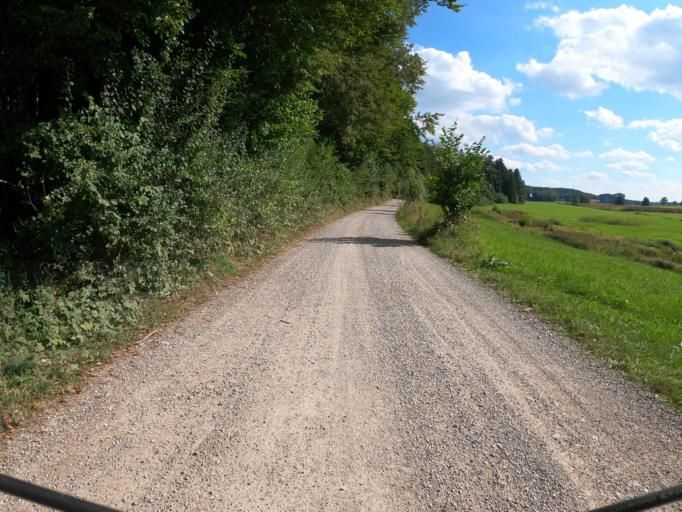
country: DE
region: Bavaria
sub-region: Swabia
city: Roggenburg
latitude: 48.3221
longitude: 10.2385
